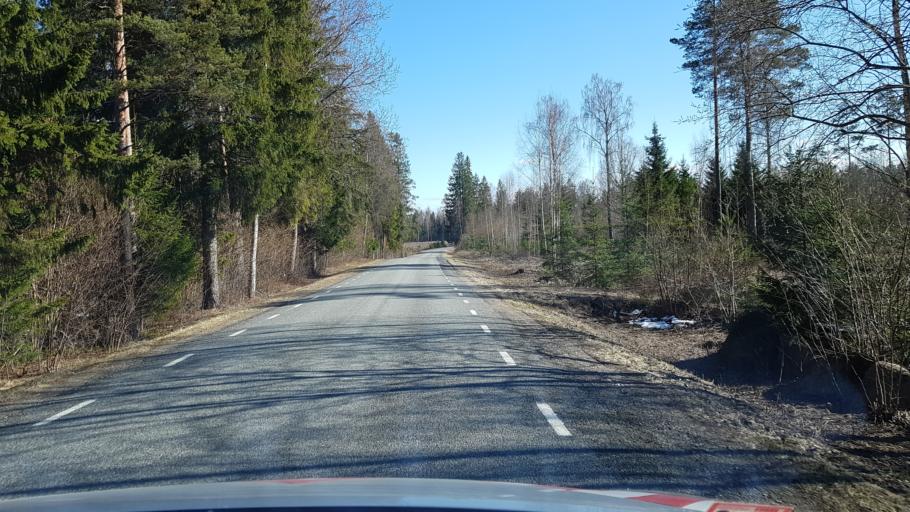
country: EE
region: Laeaene-Virumaa
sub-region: Kadrina vald
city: Kadrina
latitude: 59.3917
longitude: 26.0191
